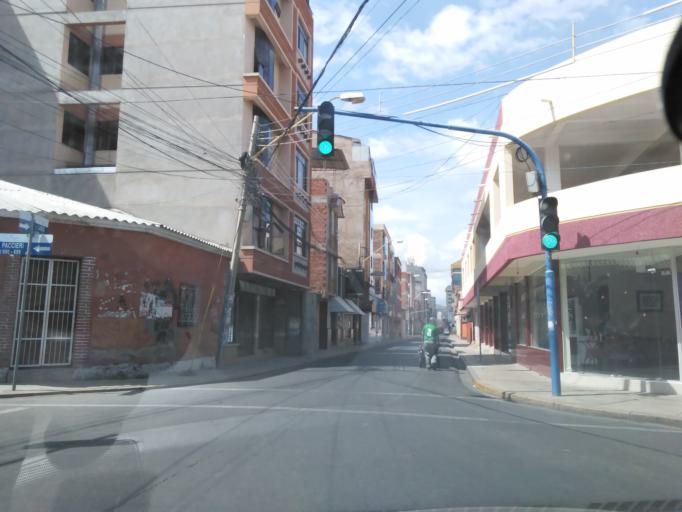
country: BO
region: Cochabamba
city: Cochabamba
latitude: -17.3872
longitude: -66.1543
